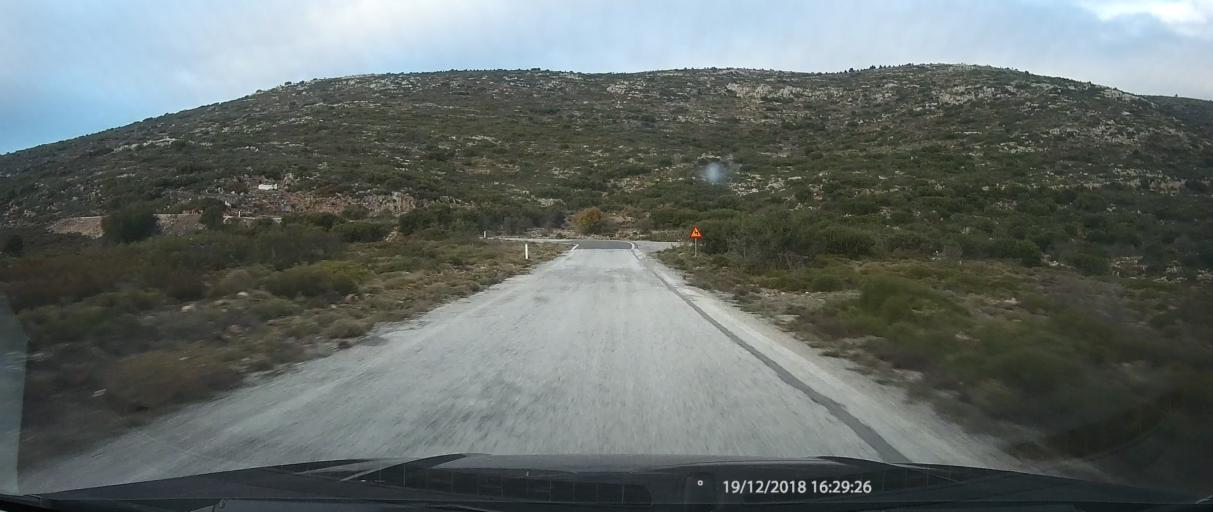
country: GR
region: Peloponnese
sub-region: Nomos Lakonias
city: Molaoi
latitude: 36.9620
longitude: 22.8752
